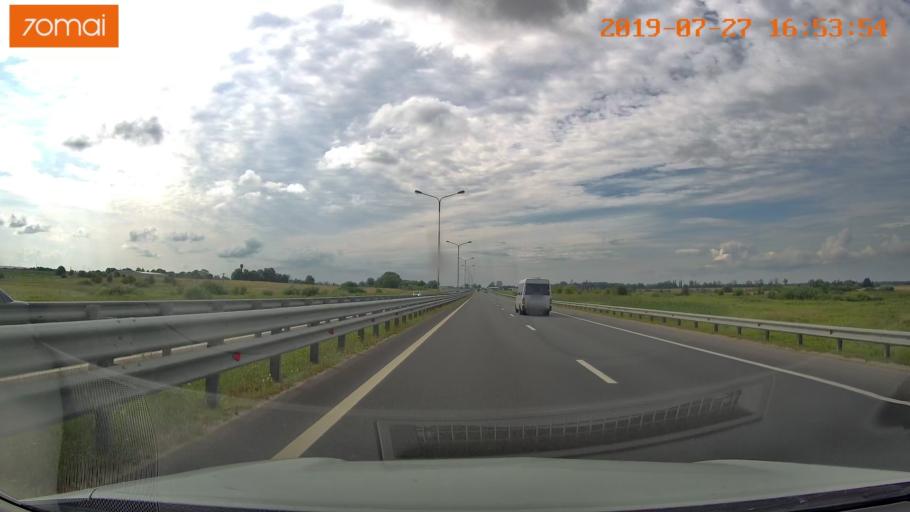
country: RU
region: Kaliningrad
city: Bol'shoe Isakovo
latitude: 54.6909
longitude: 20.8211
